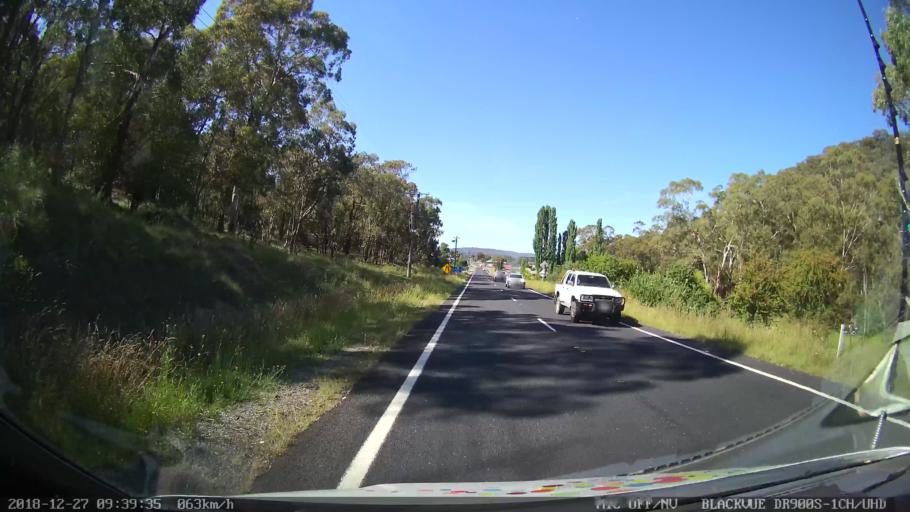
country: AU
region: New South Wales
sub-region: Lithgow
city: Portland
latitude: -33.2942
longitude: 150.0346
